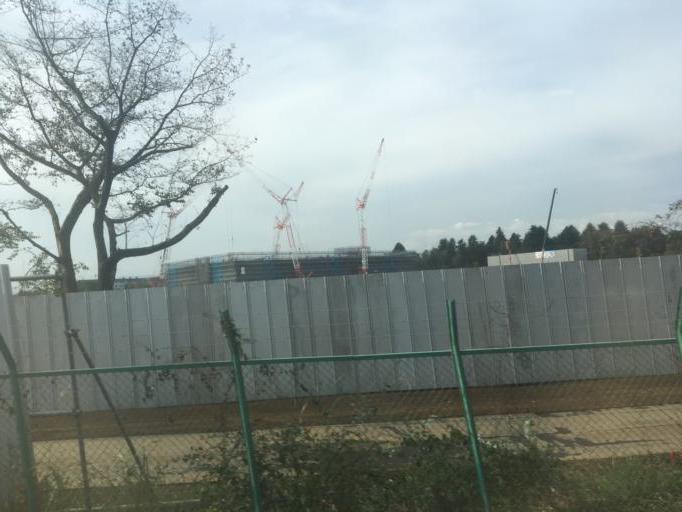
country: JP
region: Saitama
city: Sayama
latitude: 35.8390
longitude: 139.4057
